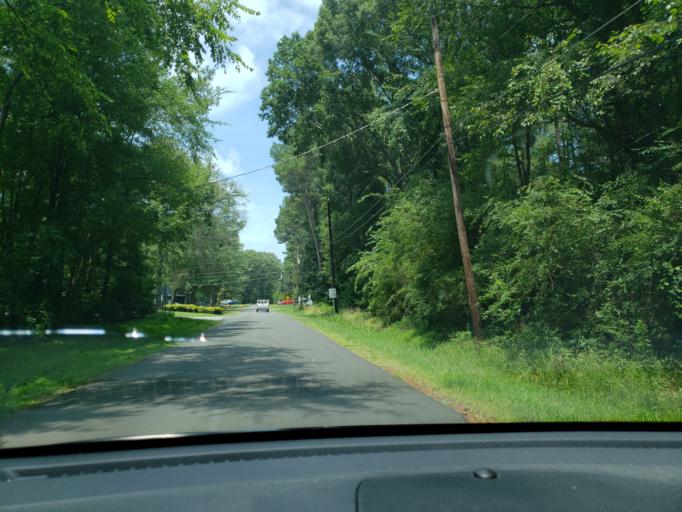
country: US
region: North Carolina
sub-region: Orange County
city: Chapel Hill
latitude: 35.9866
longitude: -78.9982
